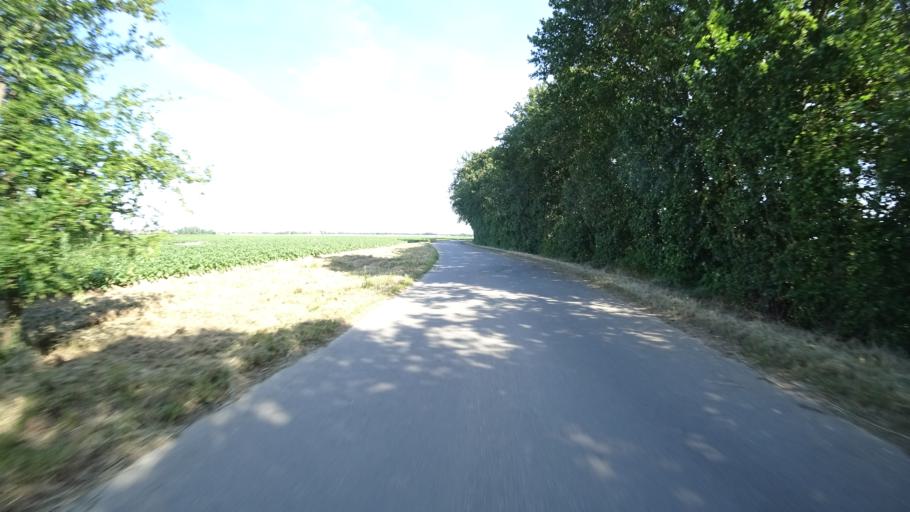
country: DE
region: North Rhine-Westphalia
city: Erwitte
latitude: 51.6160
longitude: 8.3740
